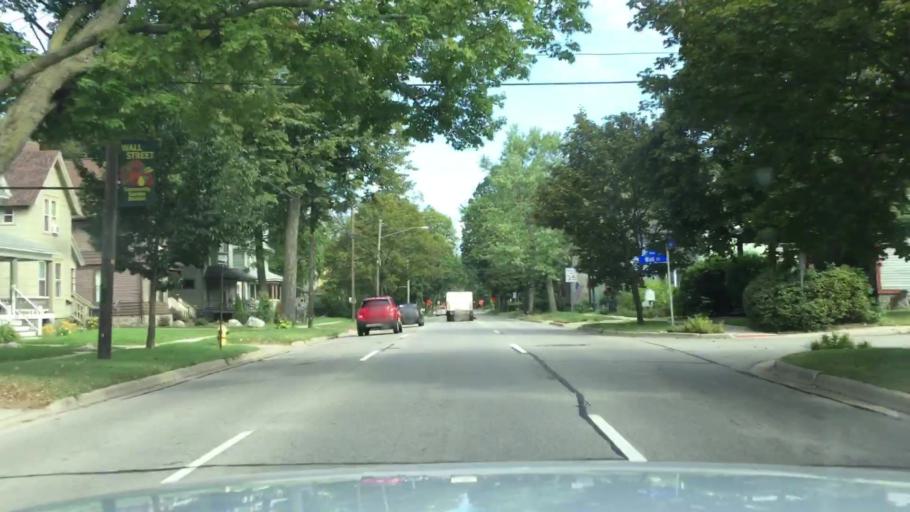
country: US
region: Michigan
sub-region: Kalamazoo County
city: Kalamazoo
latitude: 42.2810
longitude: -85.5873
